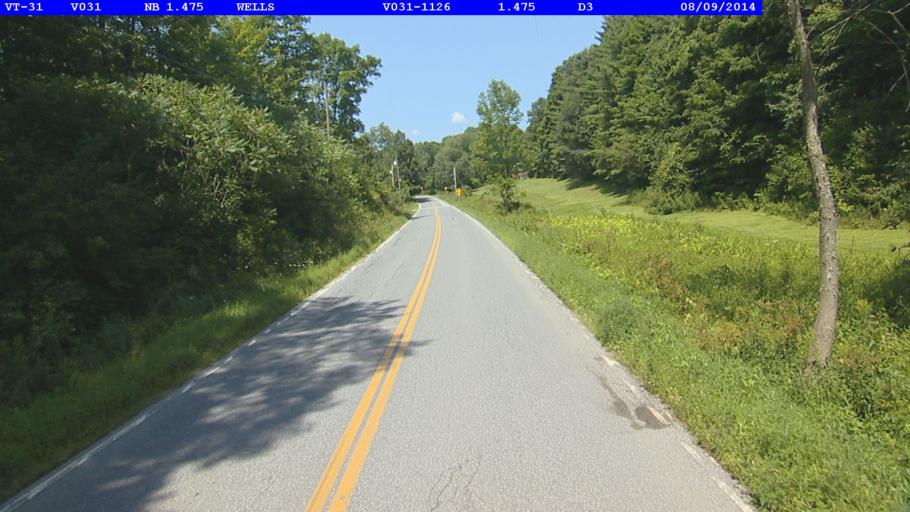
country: US
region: New York
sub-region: Washington County
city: Granville
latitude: 43.4583
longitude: -73.2415
